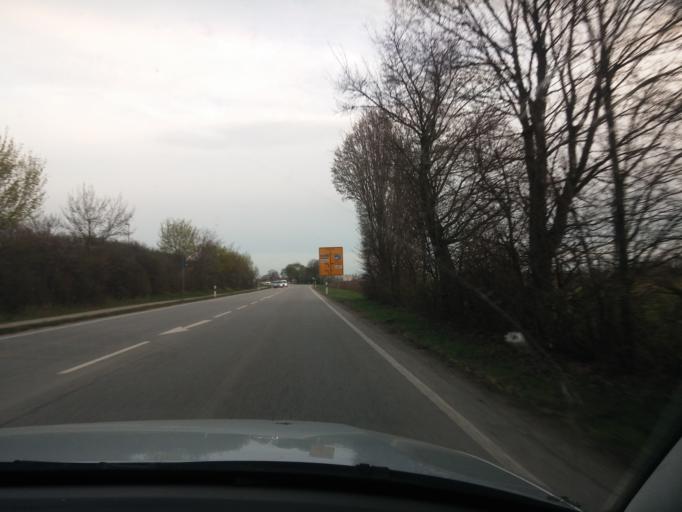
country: DE
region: Bavaria
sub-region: Upper Bavaria
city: Aschheim
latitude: 48.1624
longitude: 11.7210
